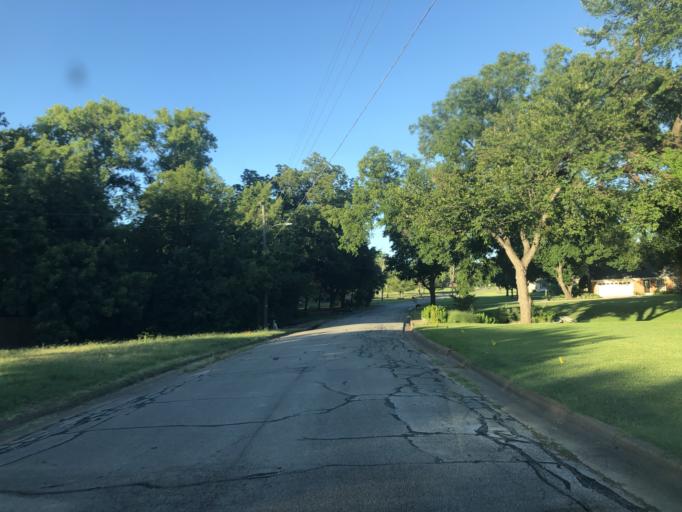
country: US
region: Texas
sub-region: Dallas County
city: Duncanville
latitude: 32.6400
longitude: -96.9385
